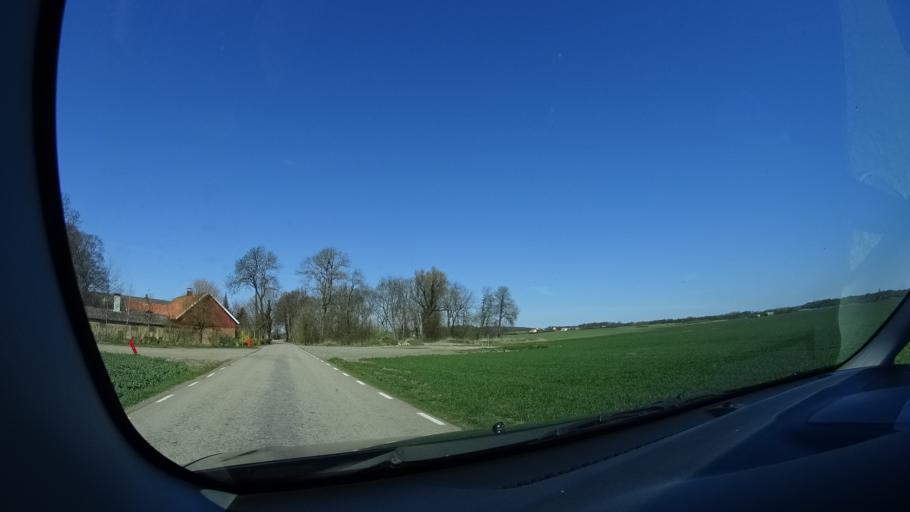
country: SE
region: Skane
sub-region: Hoganas Kommun
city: Hoganas
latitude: 56.2423
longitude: 12.5778
